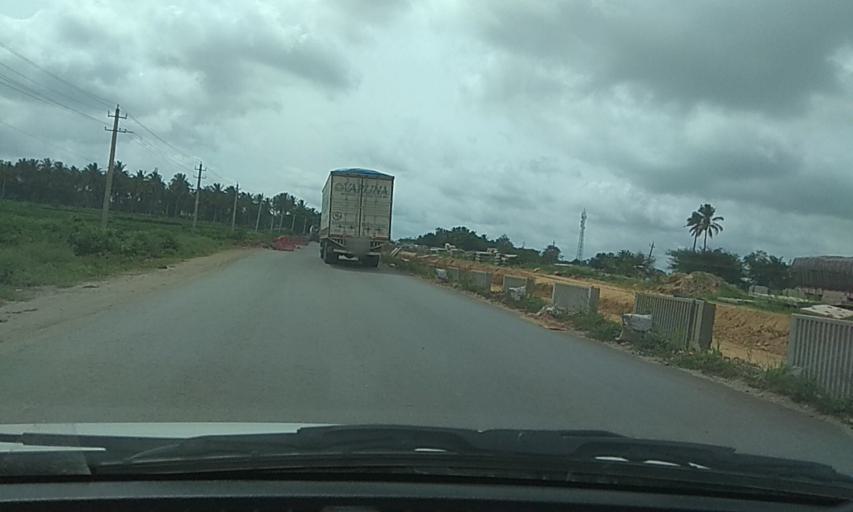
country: IN
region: Karnataka
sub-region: Davanagere
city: Mayakonda
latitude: 14.4250
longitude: 75.9748
